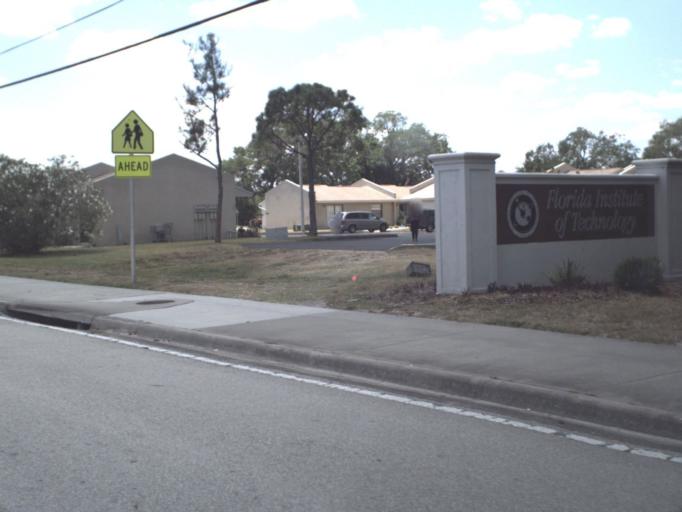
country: US
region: Florida
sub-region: Brevard County
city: Melbourne
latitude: 28.0580
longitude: -80.6215
